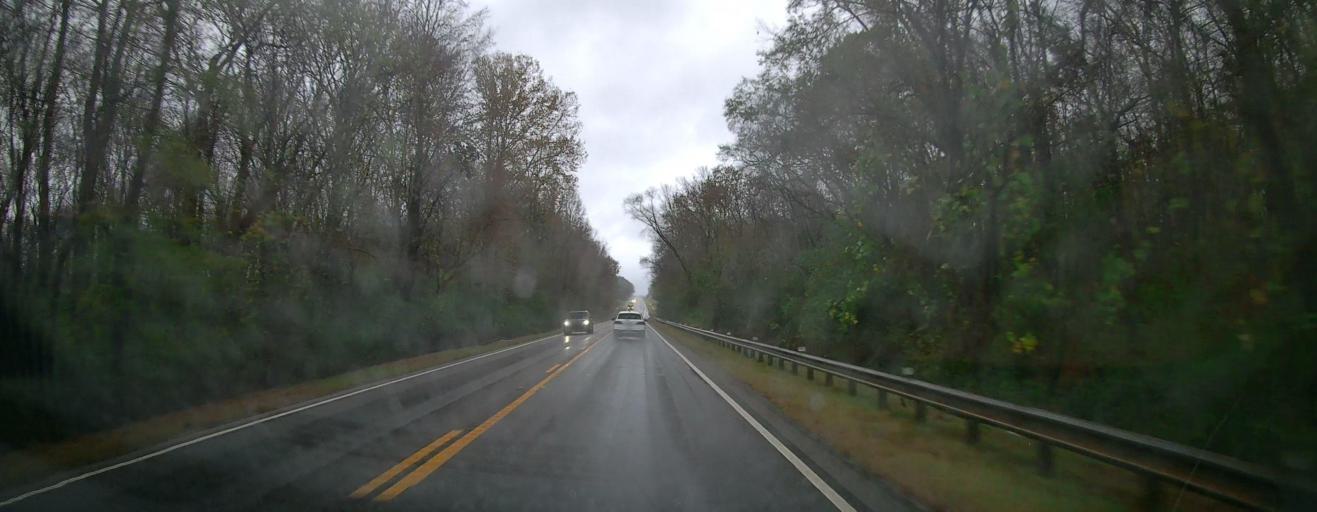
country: US
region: Georgia
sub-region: Morgan County
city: Madison
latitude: 33.6724
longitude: -83.4439
